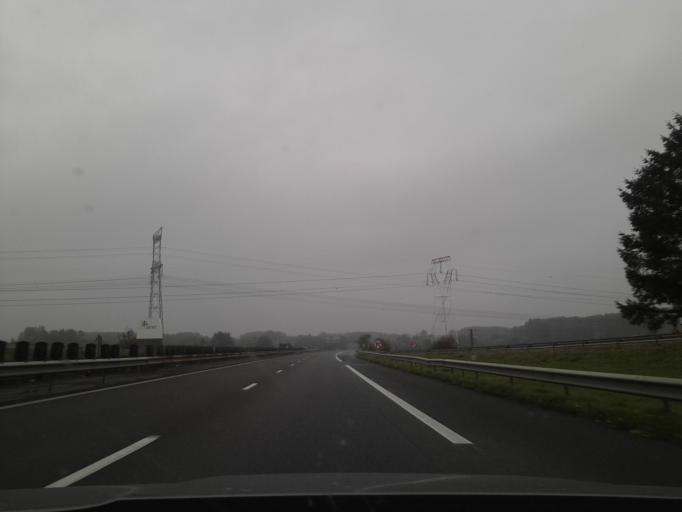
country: FR
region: Nord-Pas-de-Calais
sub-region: Departement du Nord
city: Hordain
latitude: 50.2529
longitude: 3.3204
